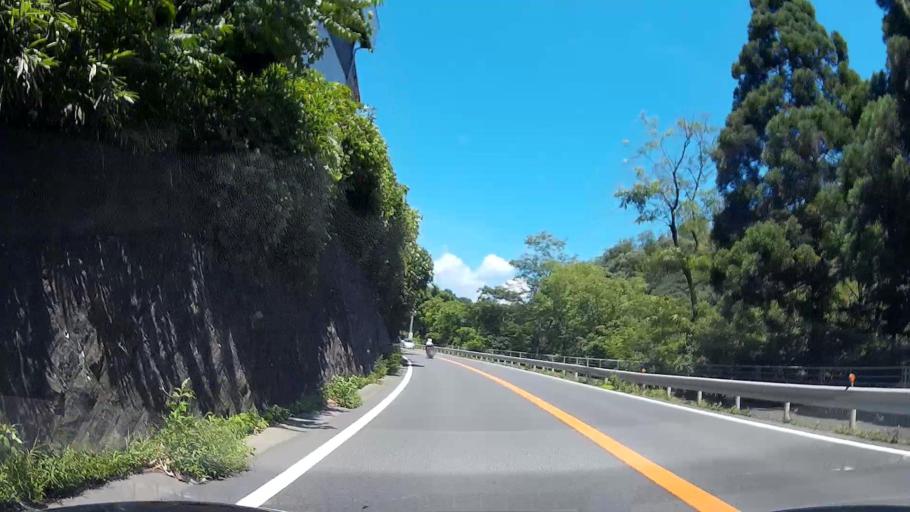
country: JP
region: Gunma
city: Numata
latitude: 36.6211
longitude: 139.0400
